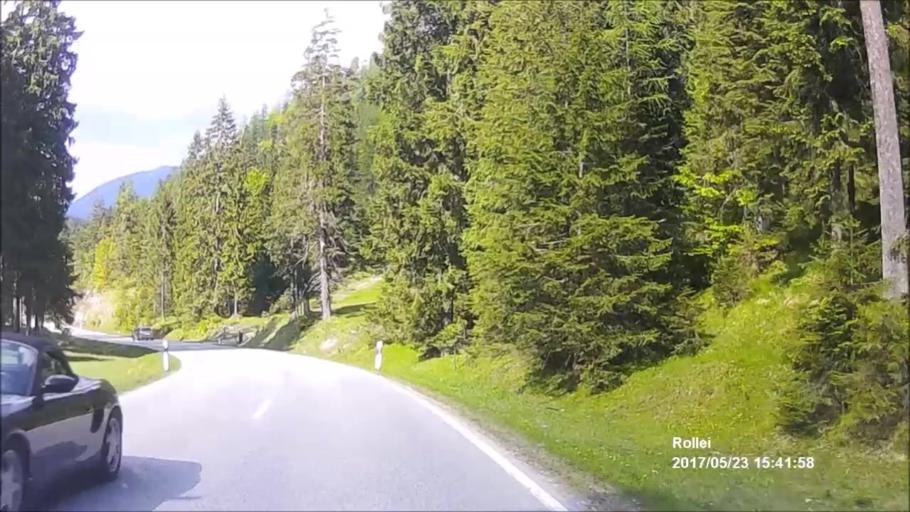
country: DE
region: Bavaria
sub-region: Upper Bavaria
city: Ramsau
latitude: 47.6301
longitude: 12.9086
